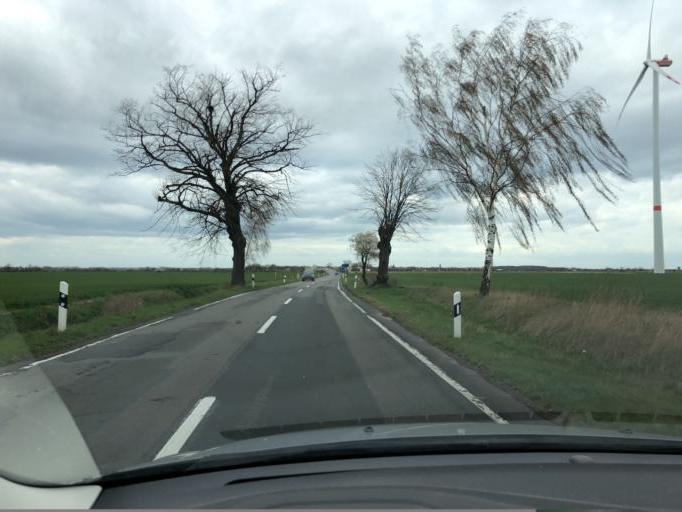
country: DE
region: Saxony-Anhalt
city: Lutzen
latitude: 51.2318
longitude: 12.1390
